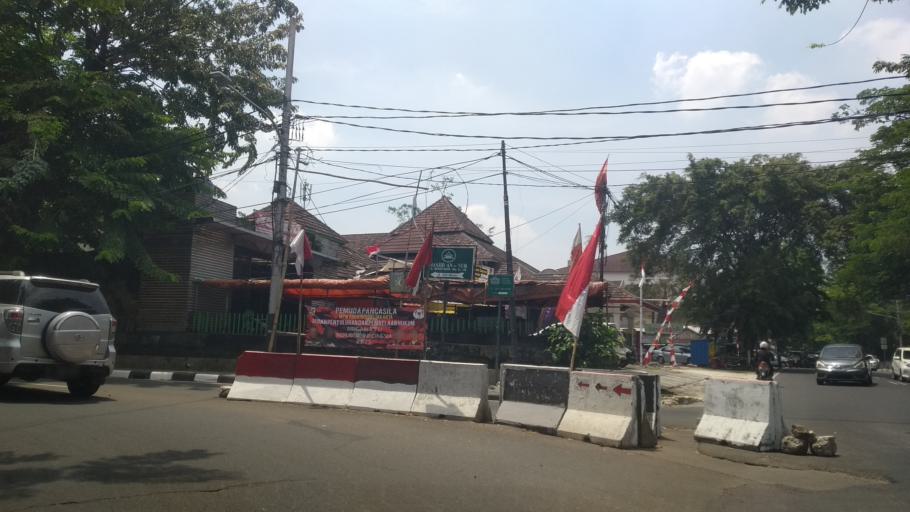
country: ID
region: Banten
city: South Tangerang
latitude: -6.2531
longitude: 106.7728
